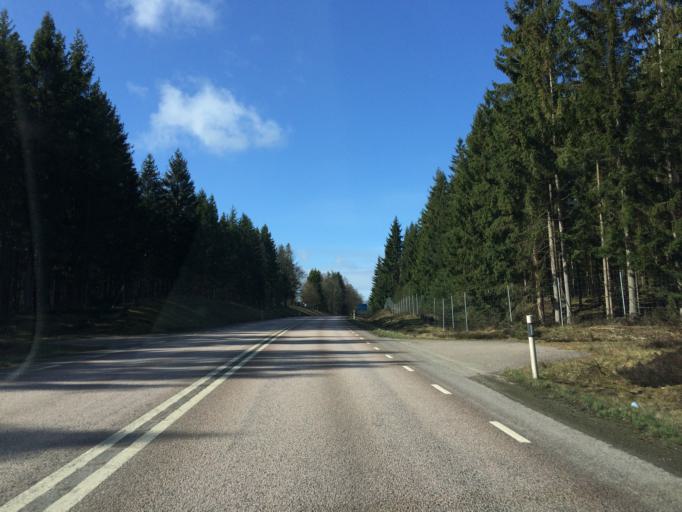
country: SE
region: Halland
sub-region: Laholms Kommun
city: Knared
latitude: 56.5230
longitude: 13.2538
